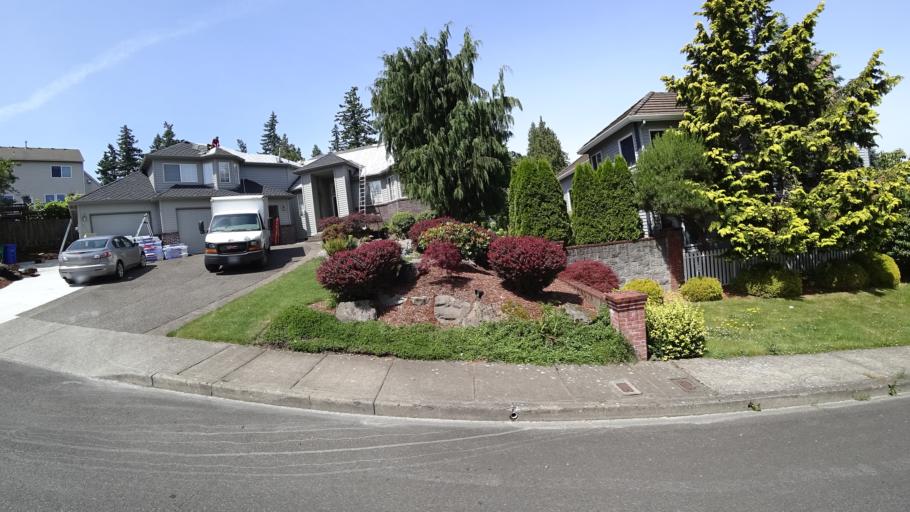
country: US
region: Oregon
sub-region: Multnomah County
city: Fairview
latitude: 45.5458
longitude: -122.5032
